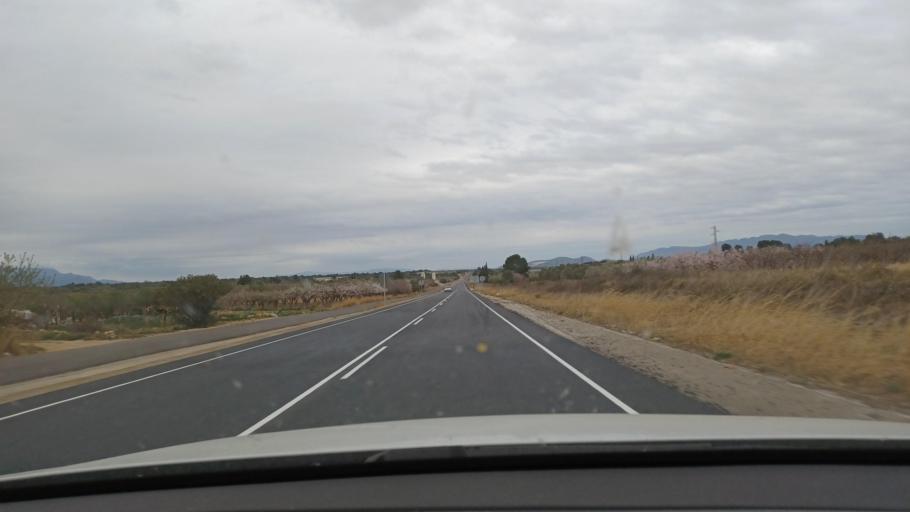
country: ES
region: Valencia
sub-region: Provincia de Castello
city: Traiguera
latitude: 40.5353
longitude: 0.3066
